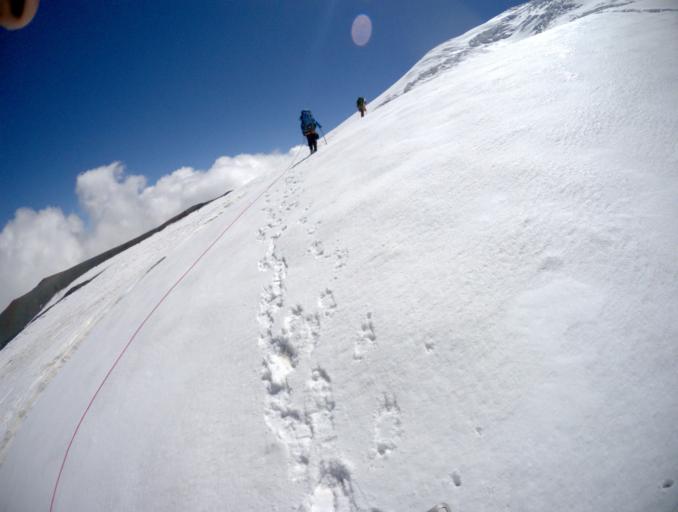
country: RU
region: Kabardino-Balkariya
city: Terskol
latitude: 43.3810
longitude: 42.4463
